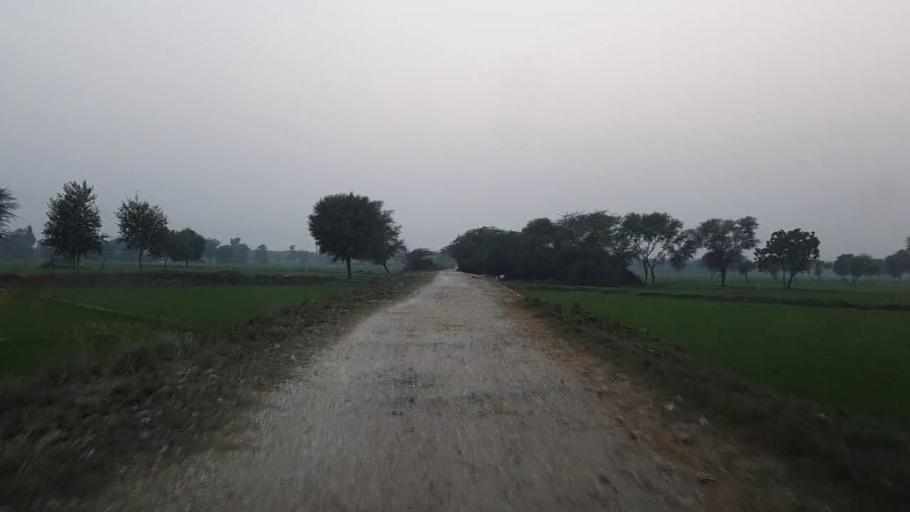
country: PK
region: Sindh
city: Kandiari
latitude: 26.9599
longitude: 68.4614
